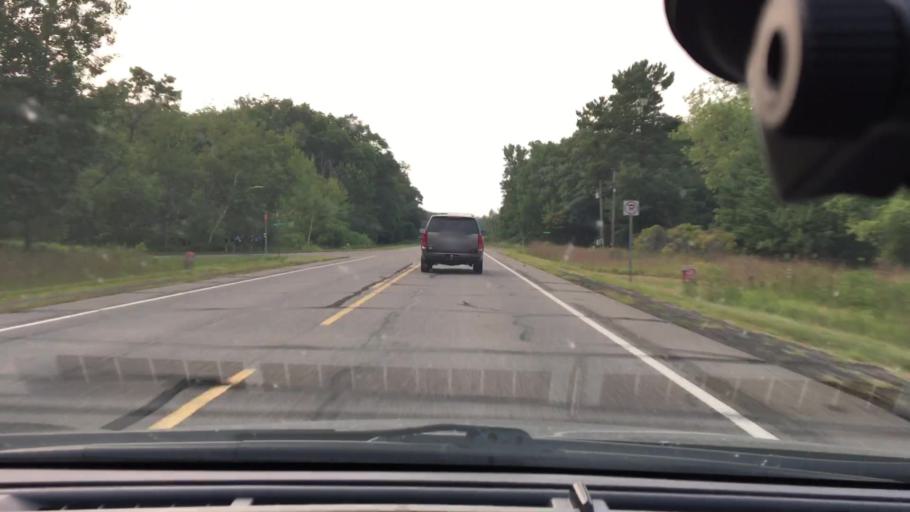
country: US
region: Minnesota
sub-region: Crow Wing County
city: Crosby
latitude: 46.3927
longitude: -93.8756
